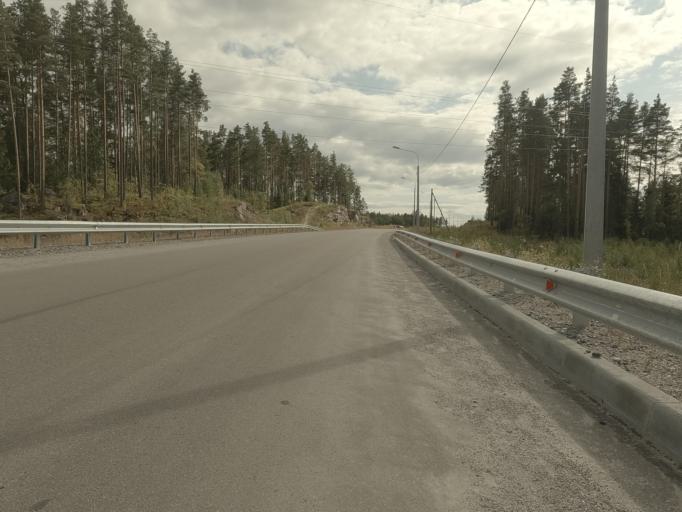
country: RU
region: Leningrad
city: Kamennogorsk
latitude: 60.9619
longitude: 29.1414
